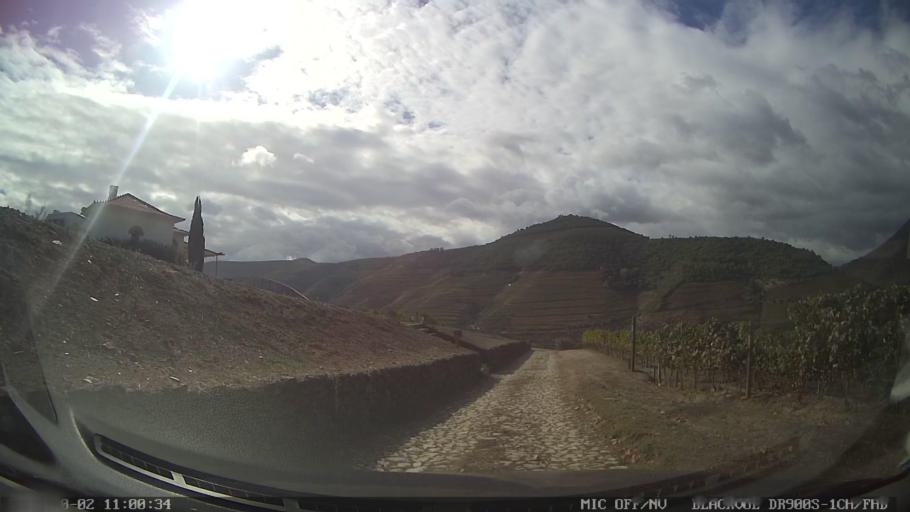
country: PT
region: Vila Real
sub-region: Sabrosa
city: Vilela
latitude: 41.1912
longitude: -7.5359
